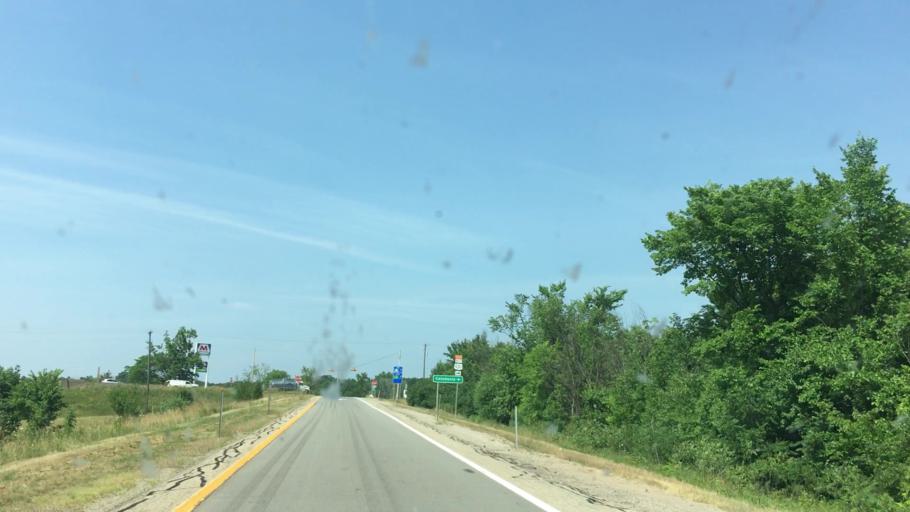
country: US
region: Michigan
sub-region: Kent County
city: Cutlerville
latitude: 42.7812
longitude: -85.6681
